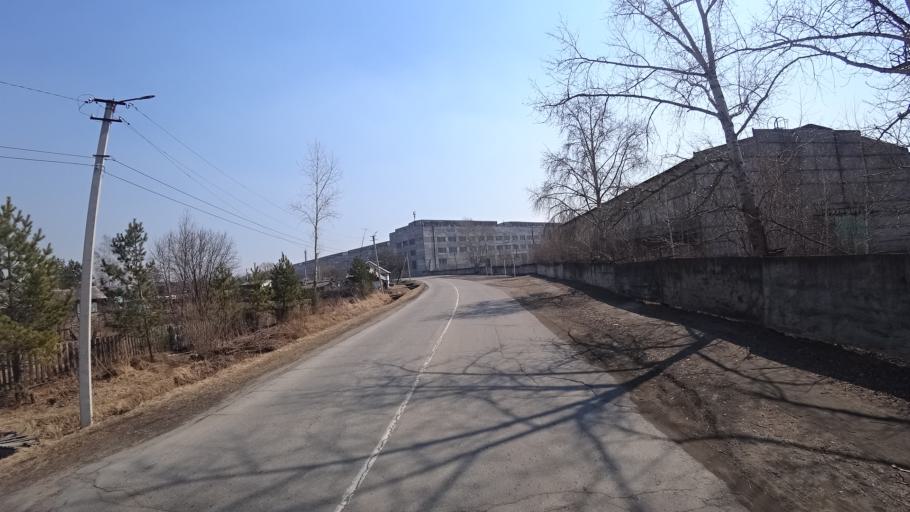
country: RU
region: Amur
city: Novobureyskiy
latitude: 49.7930
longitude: 129.8561
